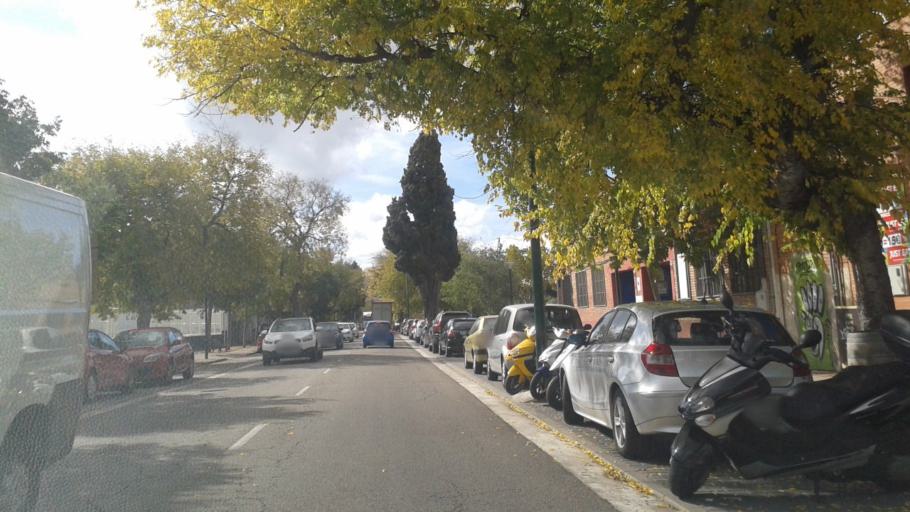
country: ES
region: Castille and Leon
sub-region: Provincia de Valladolid
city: Valladolid
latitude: 41.6638
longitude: -4.7076
